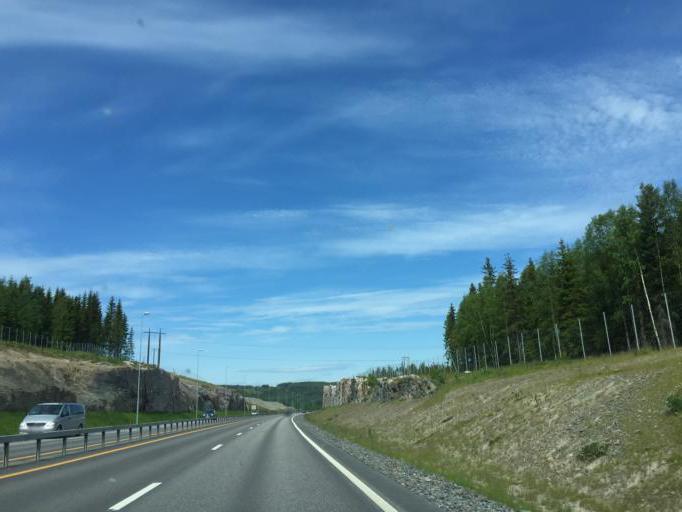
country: NO
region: Hedmark
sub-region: Kongsvinger
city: Kongsvinger
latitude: 60.2015
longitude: 11.9567
